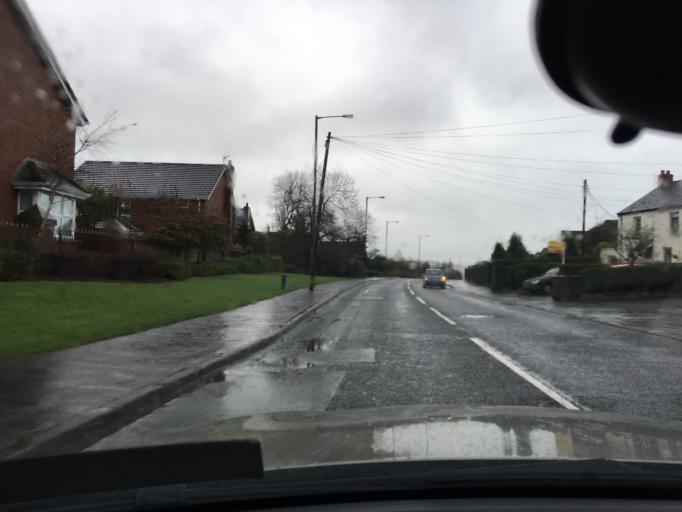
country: GB
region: Northern Ireland
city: Carnmoney
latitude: 54.6633
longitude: -5.9825
